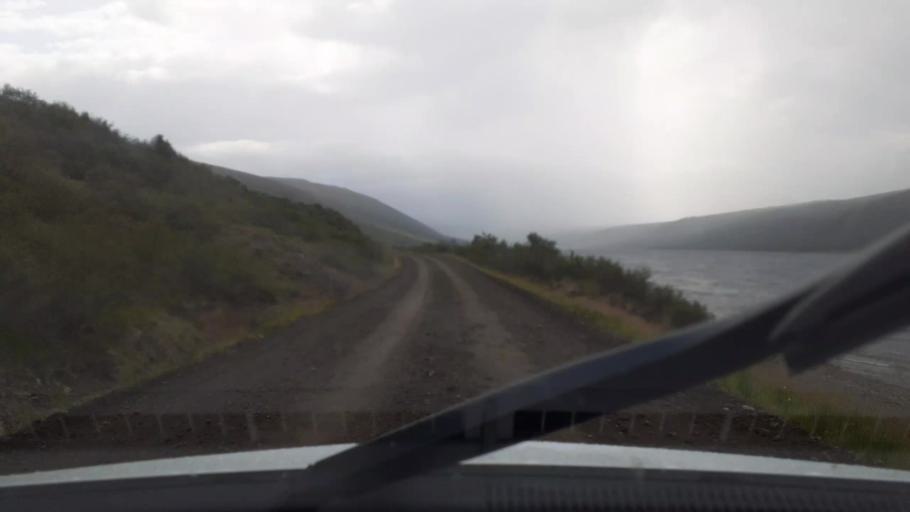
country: IS
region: Capital Region
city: Mosfellsbaer
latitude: 64.5122
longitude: -21.4025
